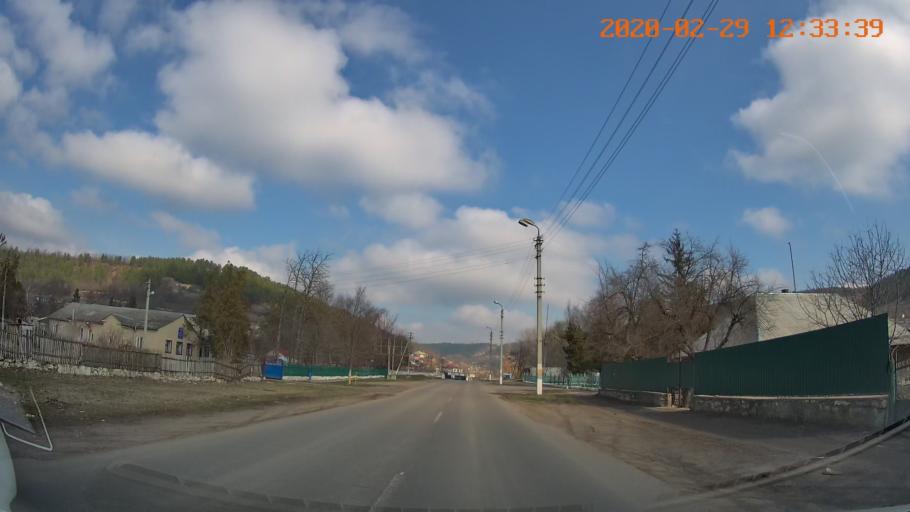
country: MD
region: Telenesti
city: Camenca
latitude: 48.0365
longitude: 28.7063
